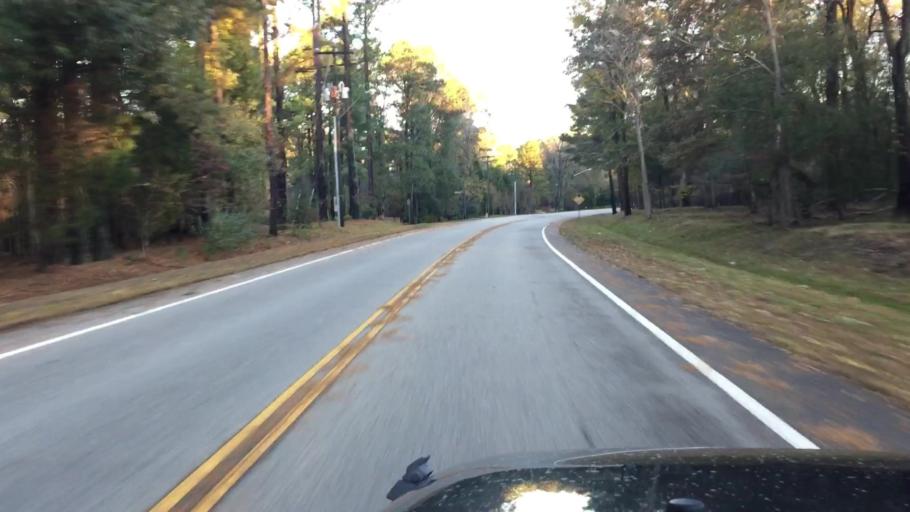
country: US
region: Virginia
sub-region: City of Williamsburg
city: Williamsburg
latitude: 37.2568
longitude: -76.7104
